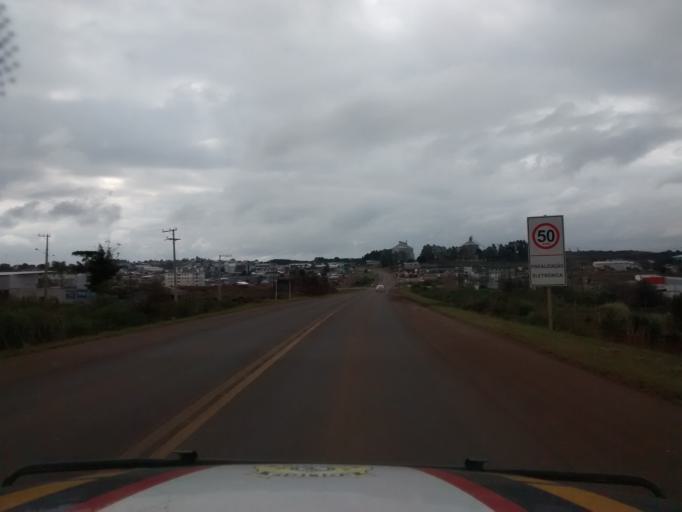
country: BR
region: Rio Grande do Sul
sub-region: Lagoa Vermelha
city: Lagoa Vermelha
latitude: -28.2186
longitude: -51.5097
